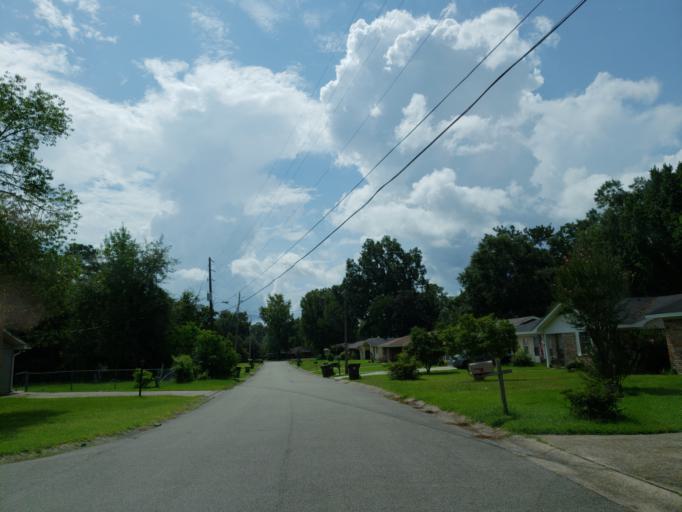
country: US
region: Mississippi
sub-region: Forrest County
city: Hattiesburg
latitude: 31.3300
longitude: -89.3240
